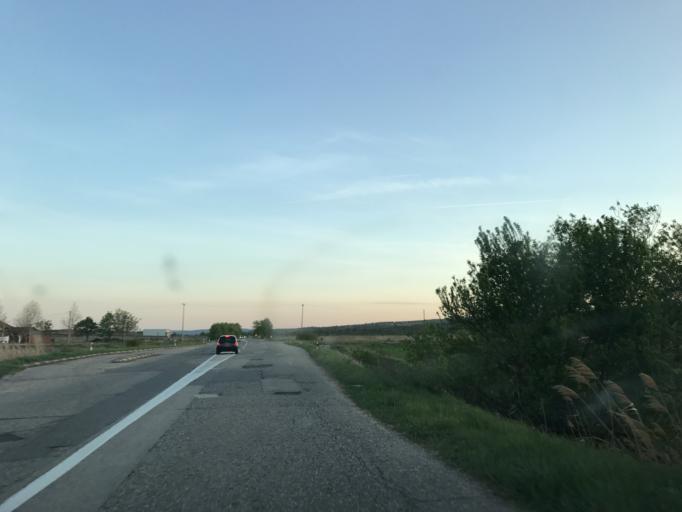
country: RS
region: Central Serbia
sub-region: Borski Okrug
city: Negotin
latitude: 44.2946
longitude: 22.5068
